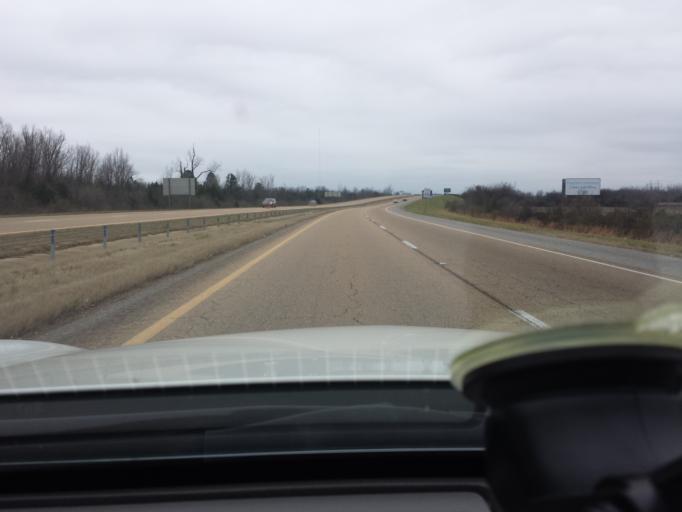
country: US
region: Mississippi
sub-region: Lee County
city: Tupelo
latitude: 34.2482
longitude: -88.6943
